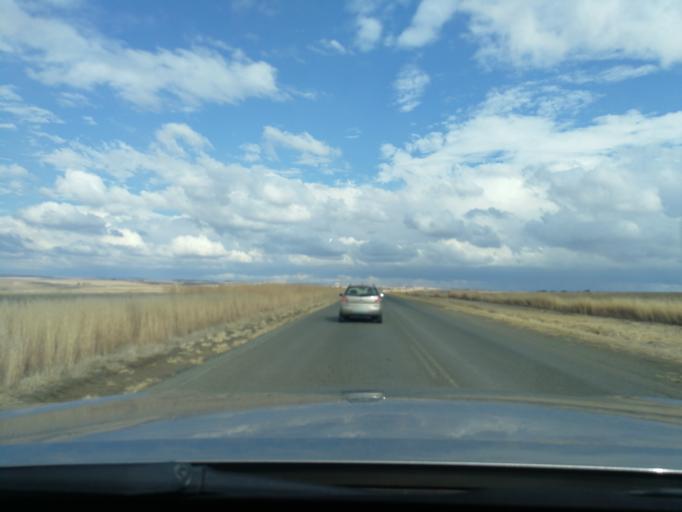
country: ZA
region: Orange Free State
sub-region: Fezile Dabi District Municipality
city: Frankfort
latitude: -27.4532
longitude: 28.5184
